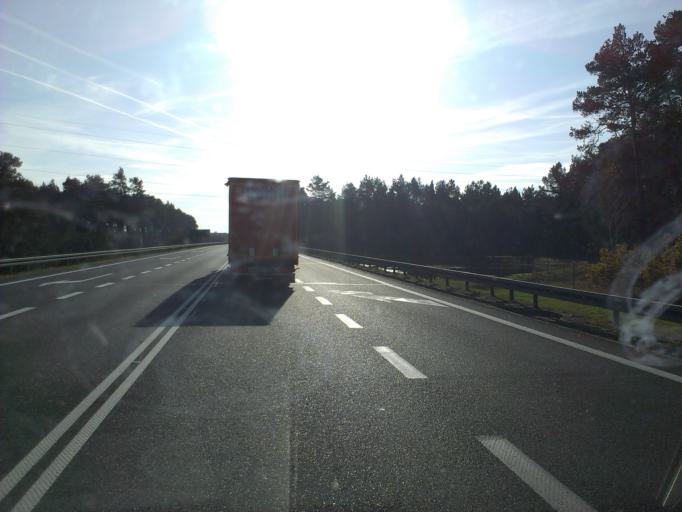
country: PL
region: Lubusz
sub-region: Powiat nowosolski
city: Nowa Sol
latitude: 51.7908
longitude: 15.6758
